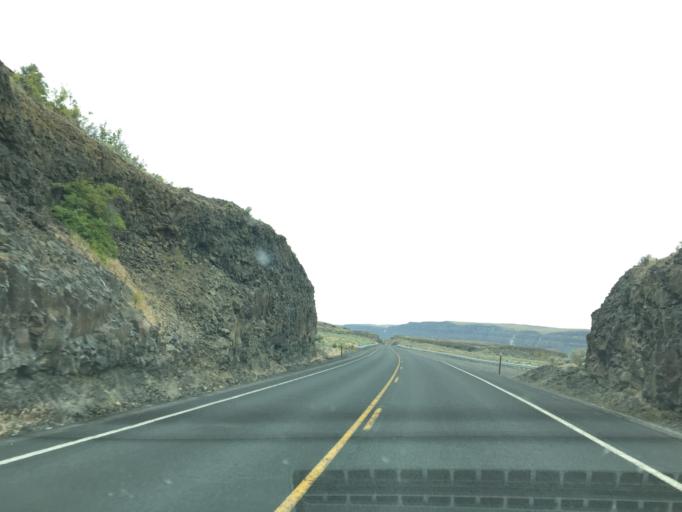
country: US
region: Washington
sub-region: Okanogan County
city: Coulee Dam
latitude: 47.7337
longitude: -119.2428
